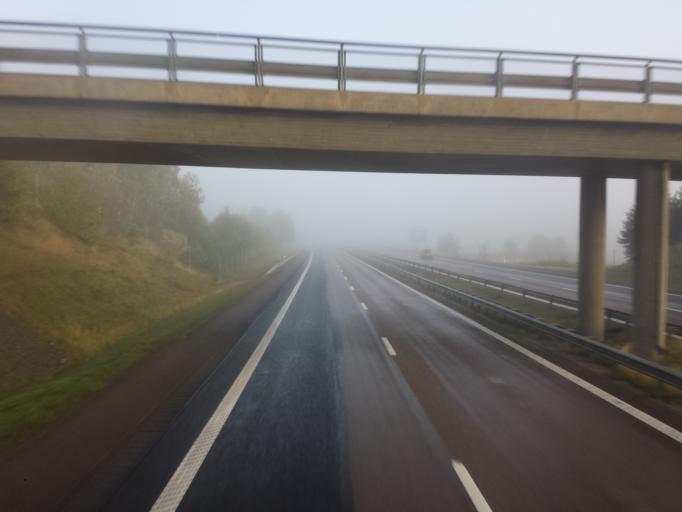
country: SE
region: Halland
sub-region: Kungsbacka Kommun
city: Fjaeras kyrkby
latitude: 57.4193
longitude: 12.1674
